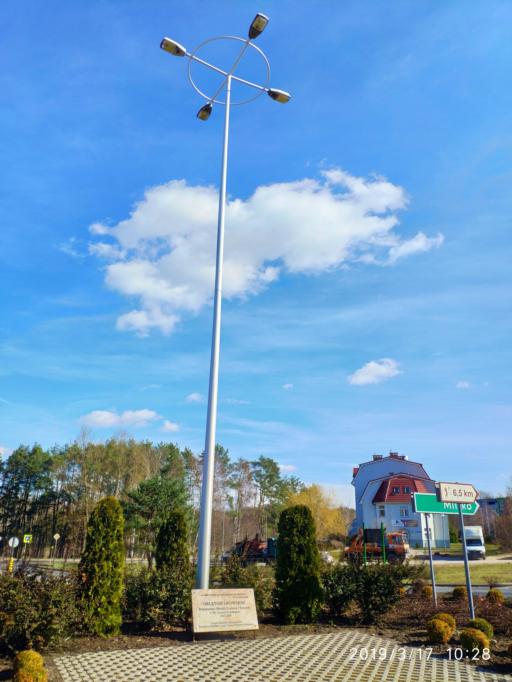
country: PL
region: Lubusz
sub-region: Zielona Gora
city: Zielona Gora
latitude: 51.9386
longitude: 15.5599
